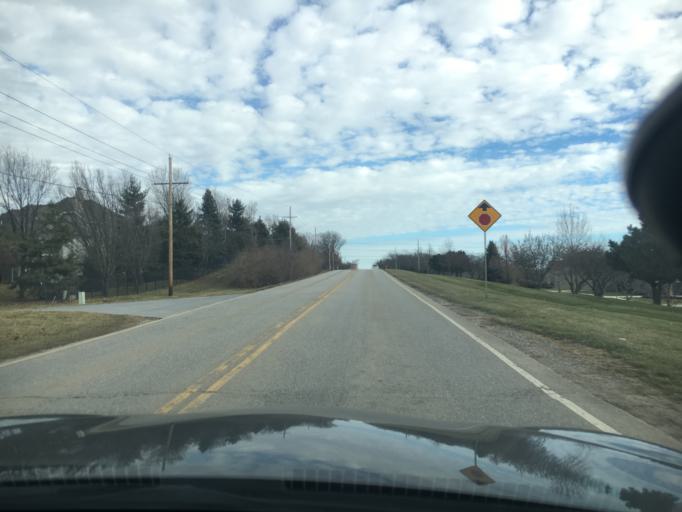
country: US
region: Missouri
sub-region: Jackson County
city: Grandview
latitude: 38.8547
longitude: -94.6337
